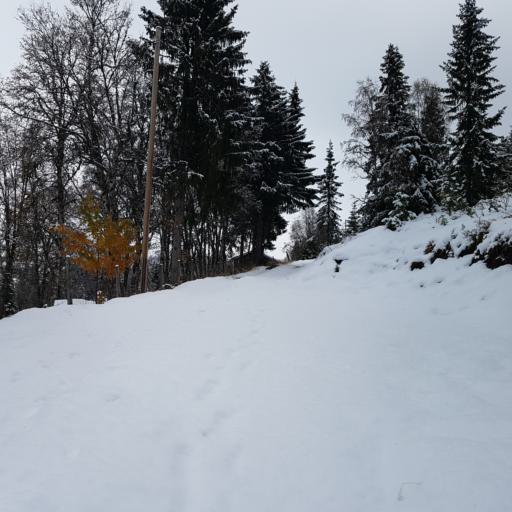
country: NO
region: Oppland
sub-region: Sel
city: Otta
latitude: 61.8079
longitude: 9.6743
